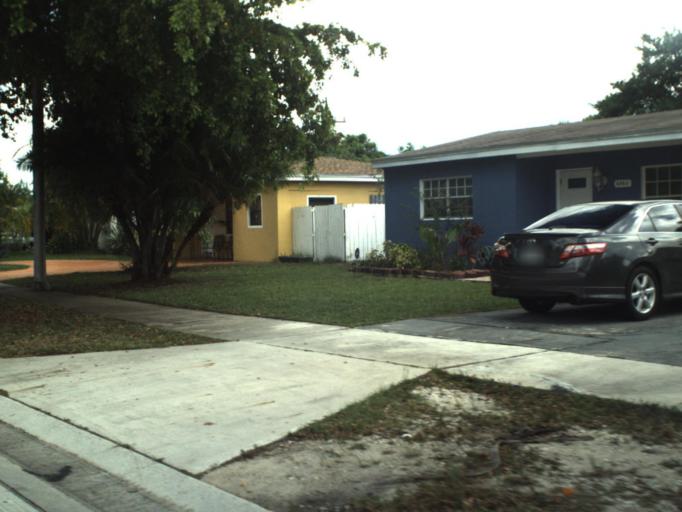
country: US
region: Florida
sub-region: Broward County
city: Miramar
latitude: 25.9836
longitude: -80.2180
